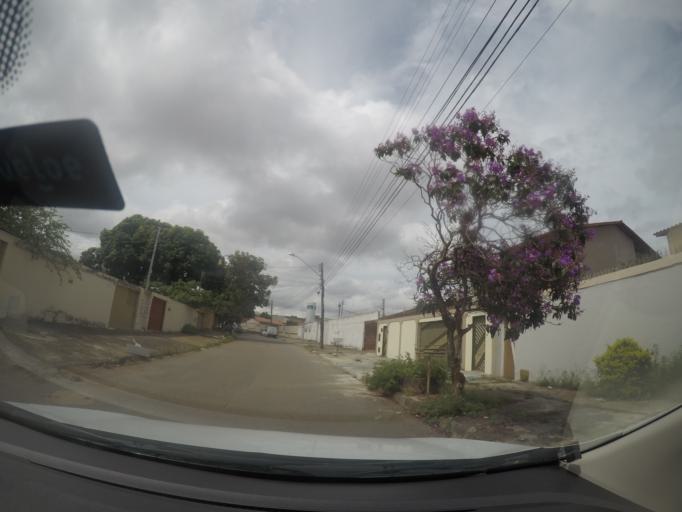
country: BR
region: Goias
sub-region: Goiania
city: Goiania
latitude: -16.7144
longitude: -49.3061
